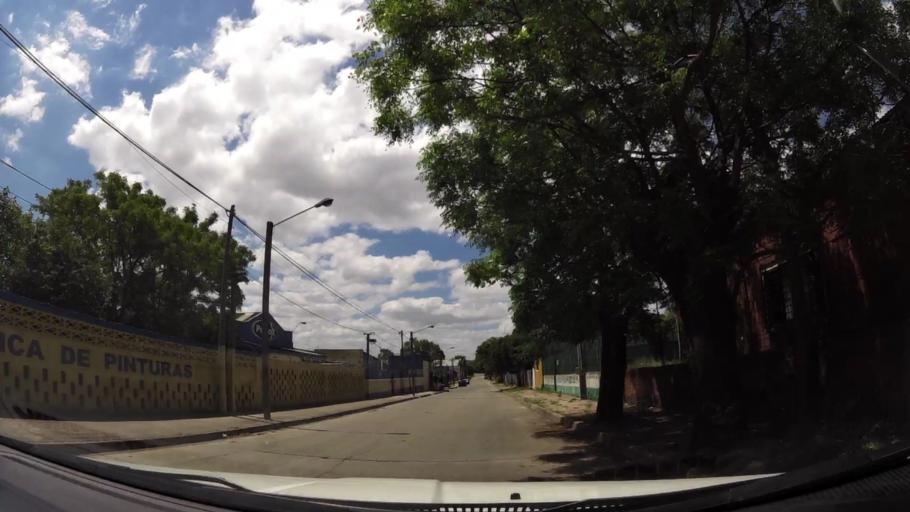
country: UY
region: Montevideo
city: Montevideo
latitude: -34.8524
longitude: -56.2380
